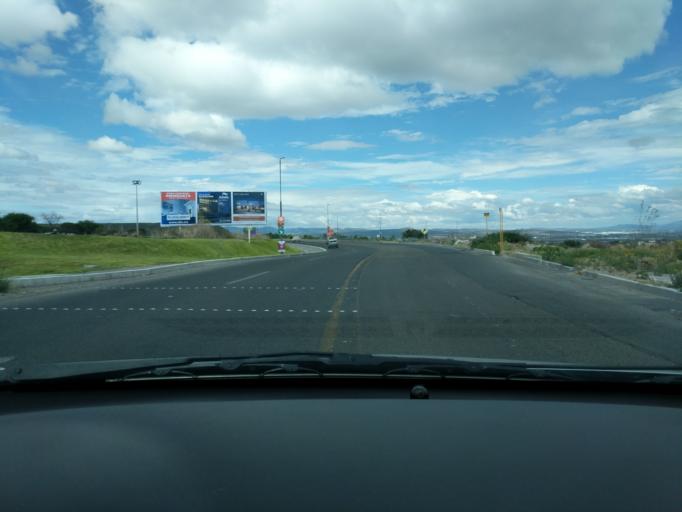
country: MX
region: Queretaro
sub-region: El Marques
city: La Pradera
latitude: 20.6691
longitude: -100.3190
